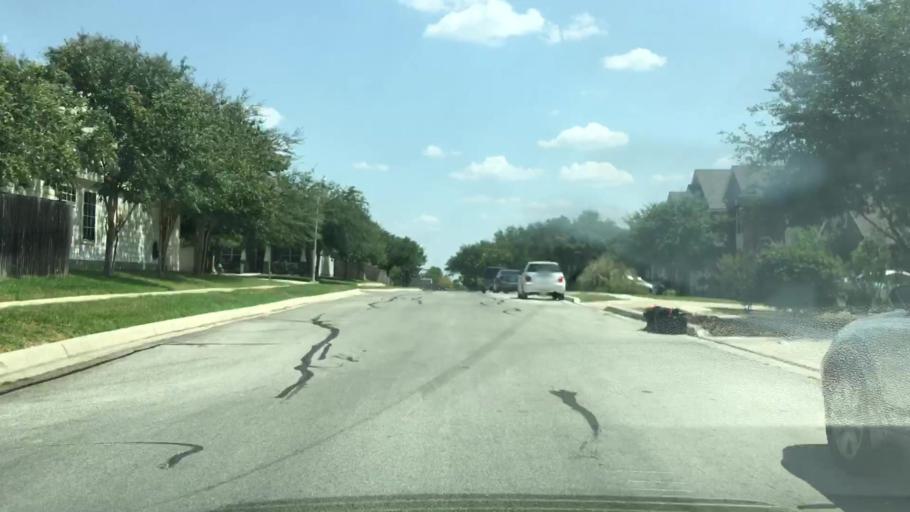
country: US
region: Texas
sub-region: Guadalupe County
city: Cibolo
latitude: 29.5818
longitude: -98.2503
